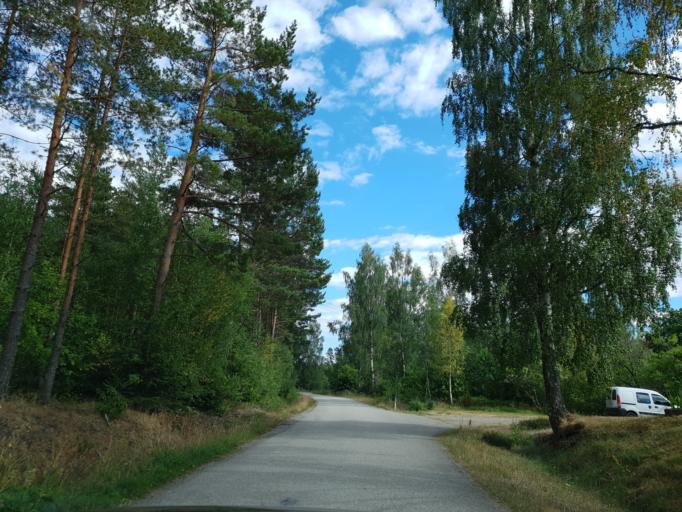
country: SE
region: Kalmar
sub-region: Emmaboda Kommun
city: Emmaboda
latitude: 56.6243
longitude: 15.6456
